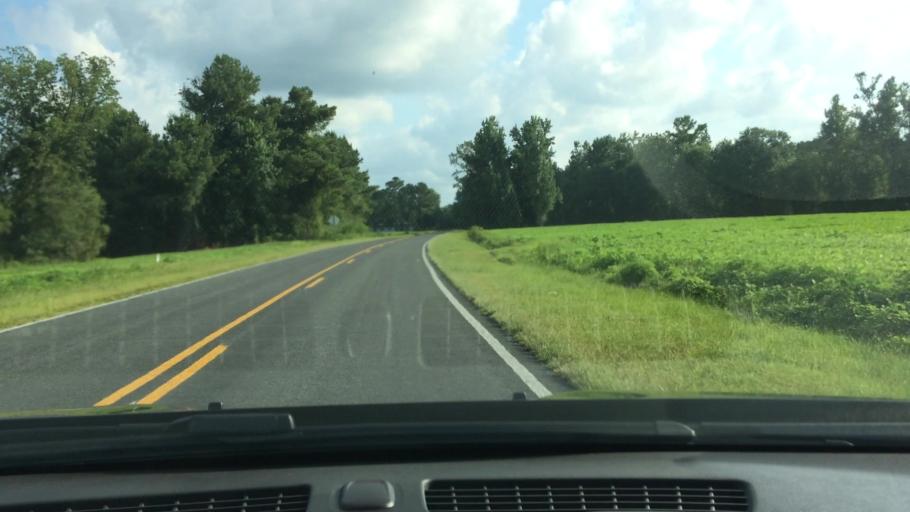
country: US
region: North Carolina
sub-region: Beaufort County
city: Washington
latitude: 35.4473
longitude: -77.1205
